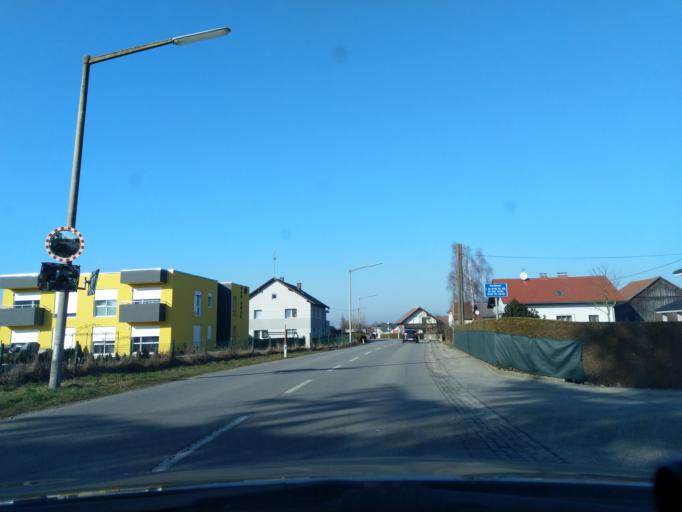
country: AT
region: Upper Austria
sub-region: Politischer Bezirk Ried im Innkreis
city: Ried im Innkreis
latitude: 48.2649
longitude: 13.4518
